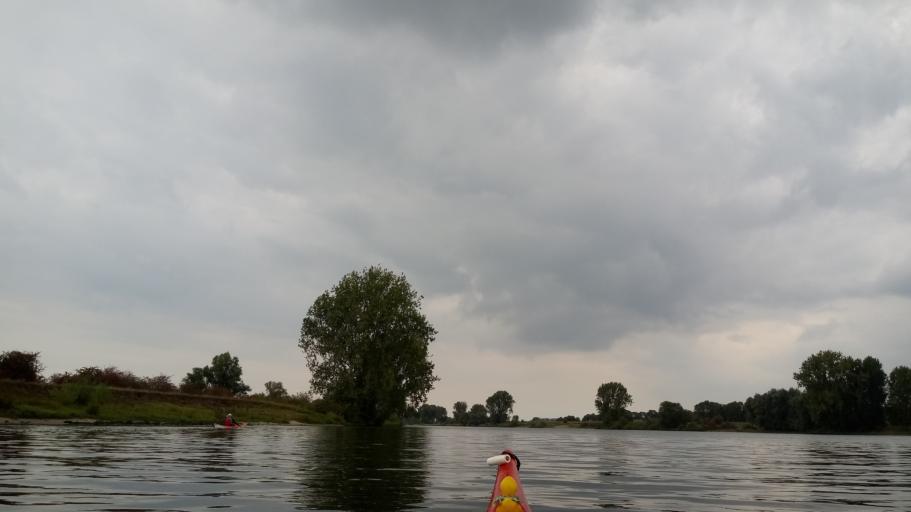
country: NL
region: Gelderland
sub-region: Gemeente Maasdriel
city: Heerewaarden
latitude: 51.7604
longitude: 5.3590
